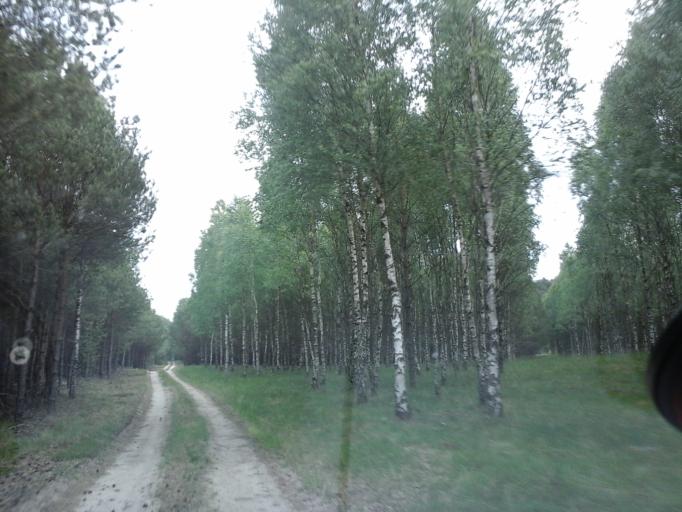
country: PL
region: West Pomeranian Voivodeship
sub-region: Powiat choszczenski
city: Drawno
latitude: 53.1220
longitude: 15.9010
